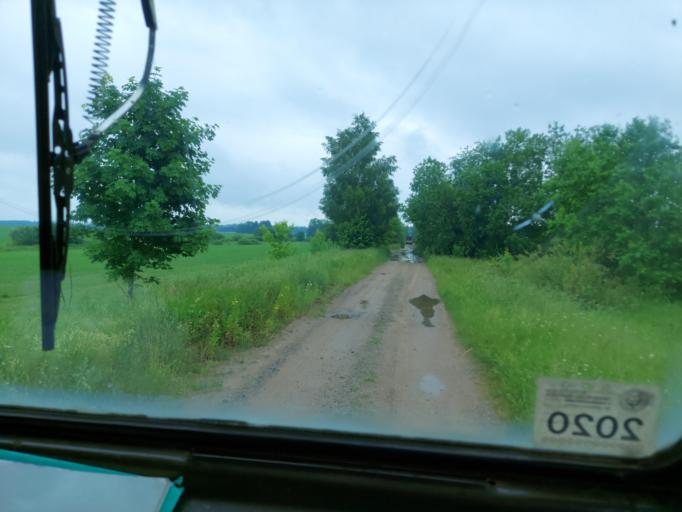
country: BY
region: Mogilev
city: Poselok Voskhod
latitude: 53.6740
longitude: 30.3900
